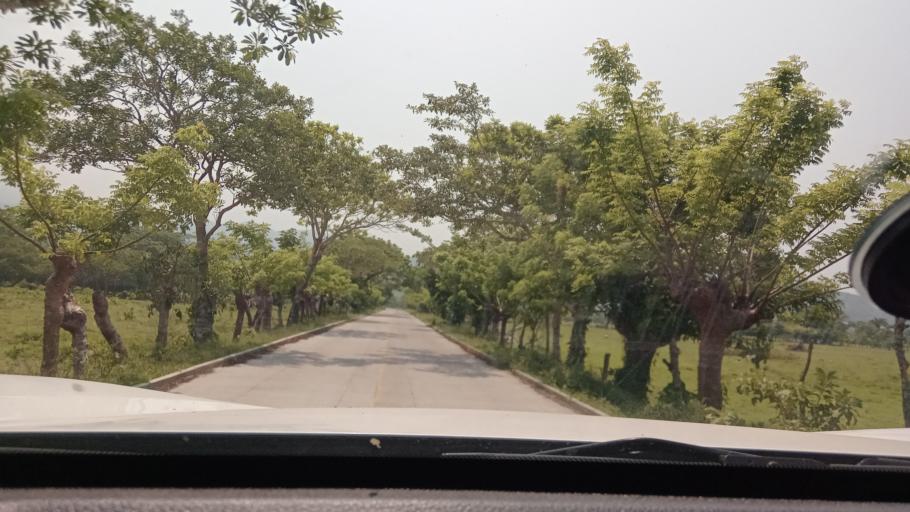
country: MX
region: Veracruz
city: Catemaco
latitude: 18.5630
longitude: -95.0480
